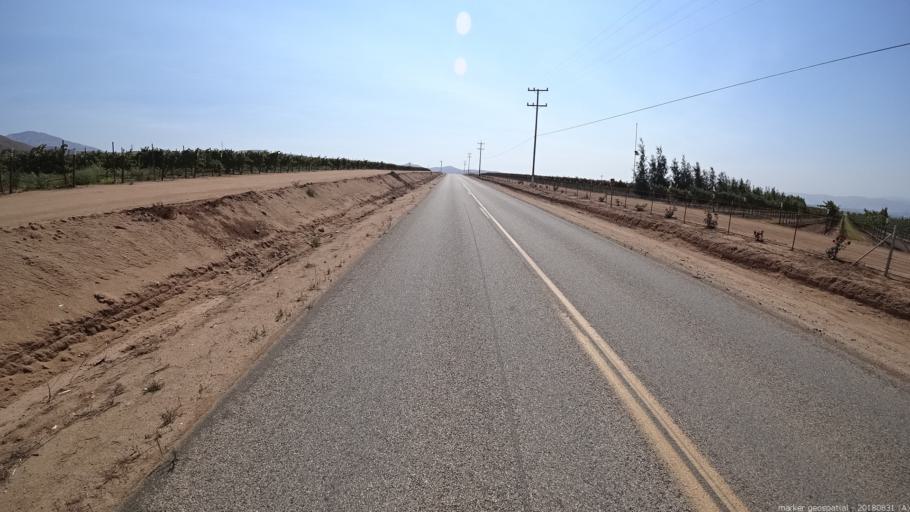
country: US
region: California
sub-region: Monterey County
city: Soledad
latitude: 36.4122
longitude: -121.2716
